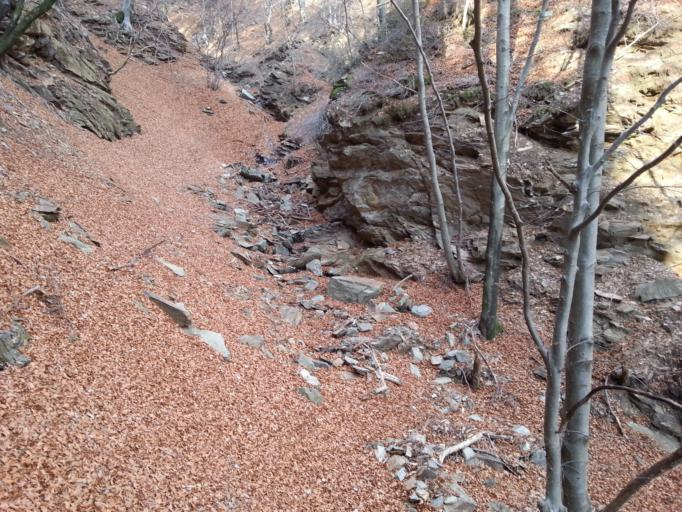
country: CH
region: Ticino
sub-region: Lugano District
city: Gravesano
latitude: 46.0575
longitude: 8.8655
